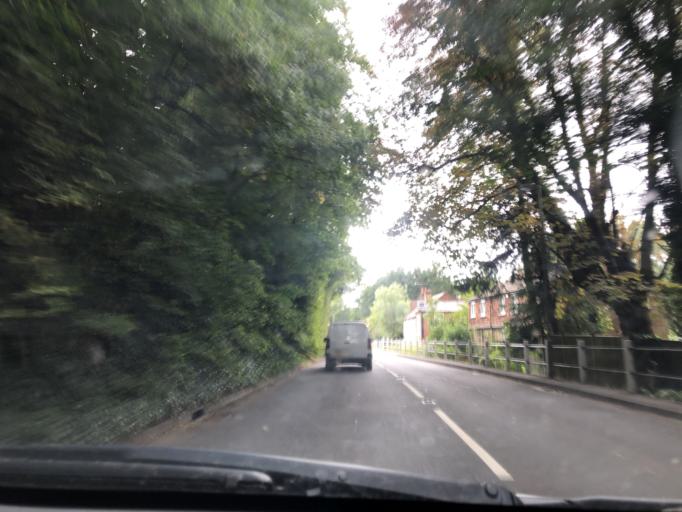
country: GB
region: England
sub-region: Kent
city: Halstead
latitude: 51.2786
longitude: 0.1290
